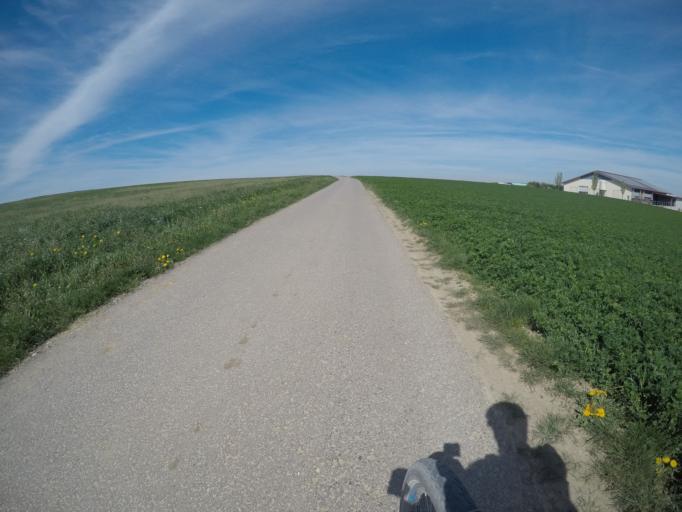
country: DE
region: Baden-Wuerttemberg
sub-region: Regierungsbezirk Stuttgart
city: Ditzingen
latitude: 48.8238
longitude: 9.0383
